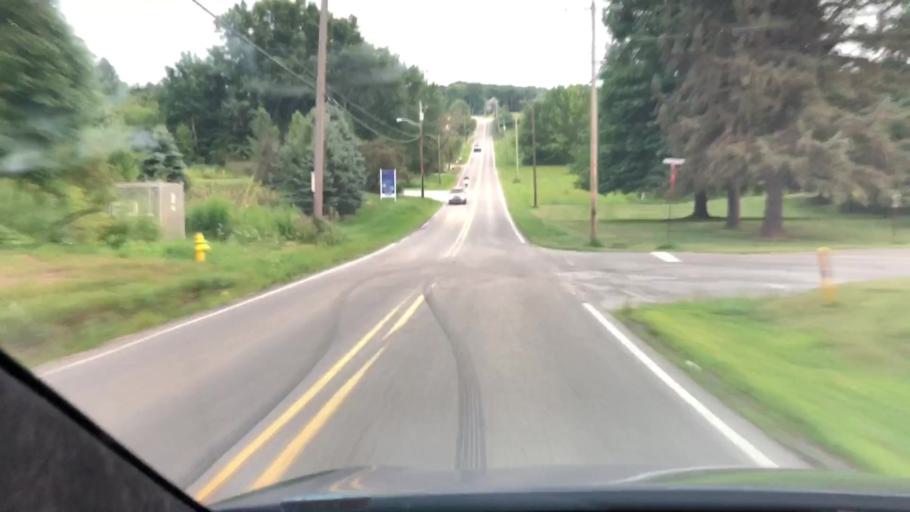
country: US
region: Pennsylvania
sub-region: Butler County
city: Shanor-Northvue
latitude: 40.8999
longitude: -79.9288
